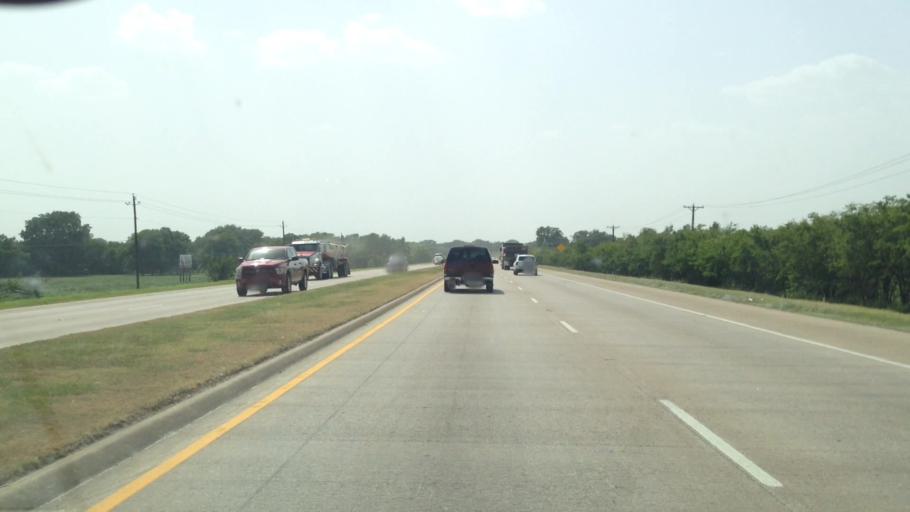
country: US
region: Texas
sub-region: Collin County
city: McKinney
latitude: 33.2024
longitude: -96.5909
